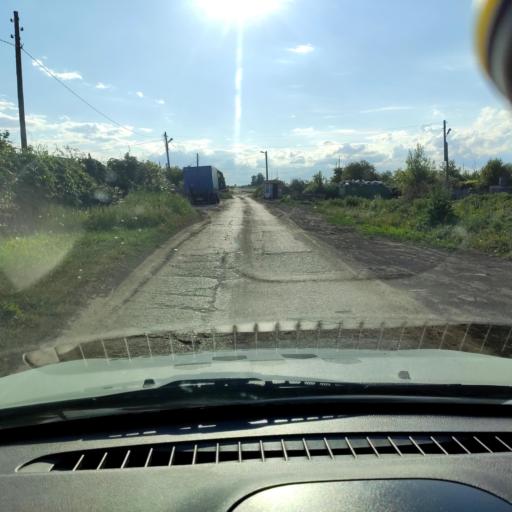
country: RU
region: Samara
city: Tol'yatti
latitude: 53.5909
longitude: 49.4417
